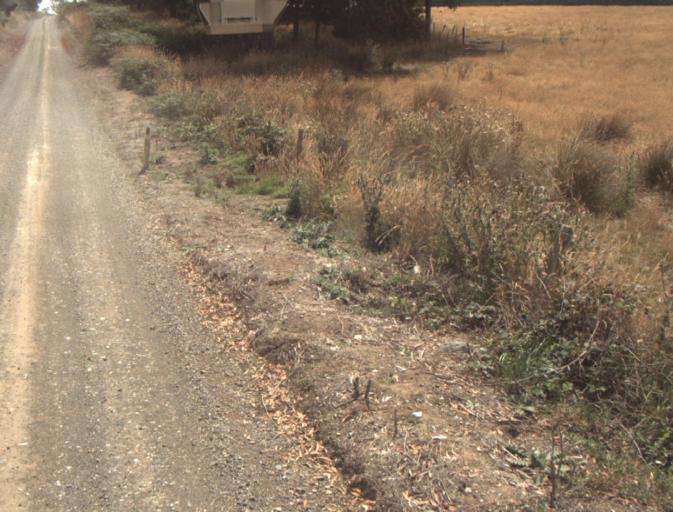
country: AU
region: Tasmania
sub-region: Launceston
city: Mayfield
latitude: -41.1960
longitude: 147.1699
